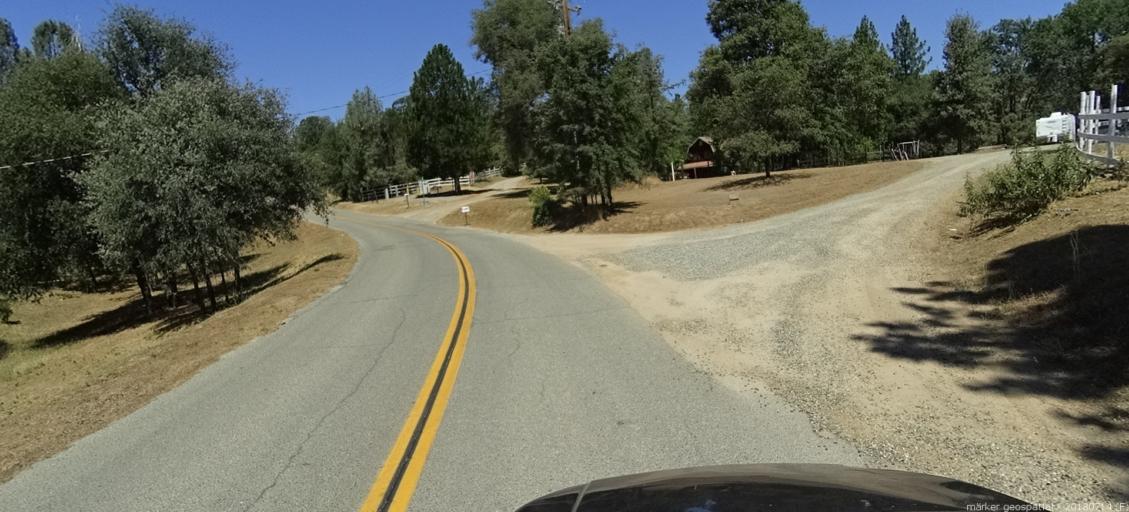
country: US
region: California
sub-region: Madera County
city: Ahwahnee
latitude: 37.3852
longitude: -119.6766
